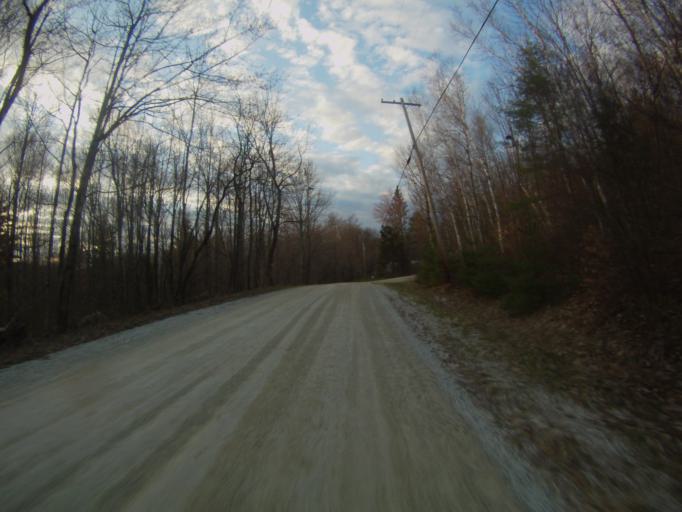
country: US
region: Vermont
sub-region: Rutland County
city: Brandon
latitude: 43.8540
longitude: -72.9989
